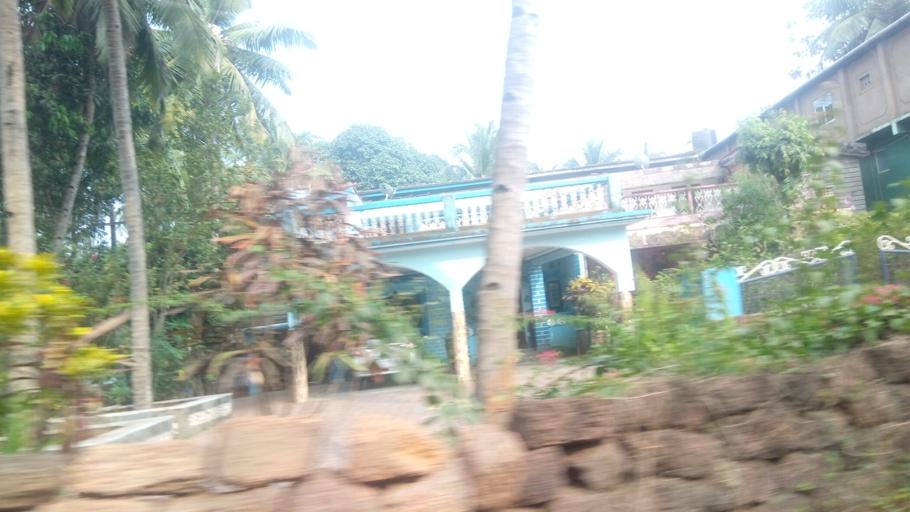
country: IN
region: Goa
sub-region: South Goa
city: Varca
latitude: 15.2440
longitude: 73.9391
